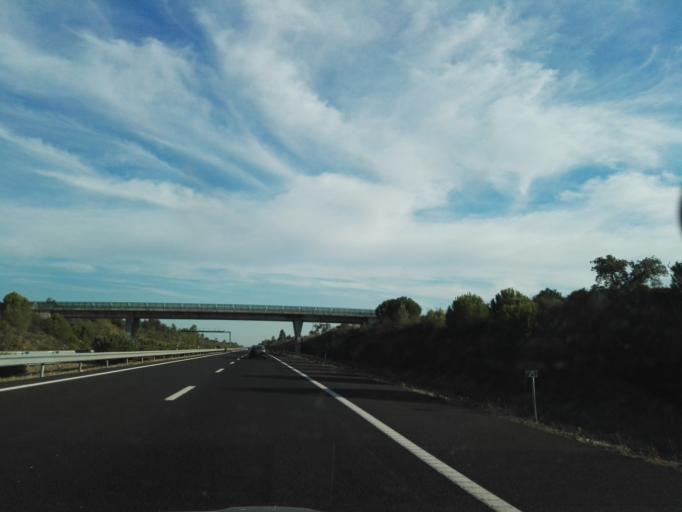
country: PT
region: Santarem
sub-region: Benavente
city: Poceirao
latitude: 38.8150
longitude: -8.7090
